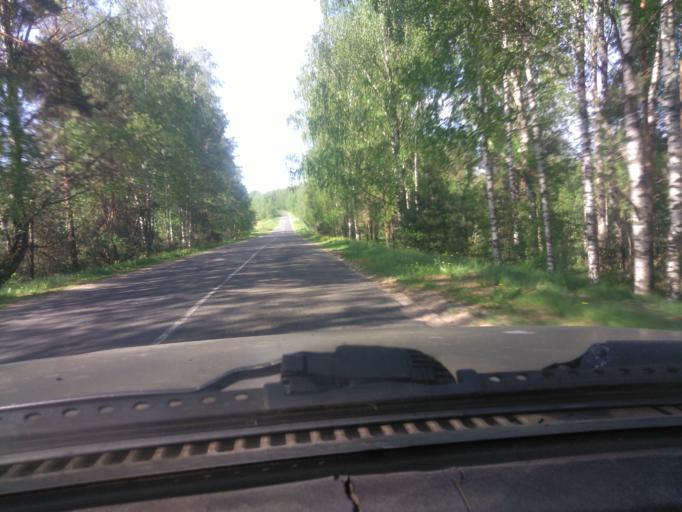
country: BY
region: Mogilev
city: Myazhysyatki
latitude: 53.8111
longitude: 30.0911
